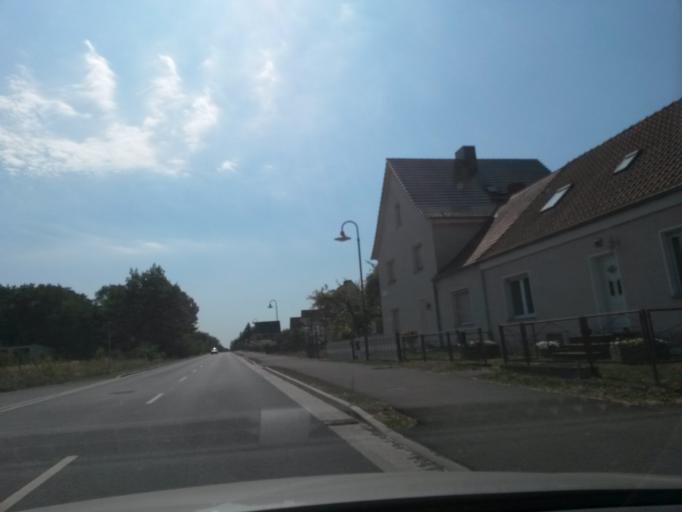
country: DE
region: Saxony-Anhalt
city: Jerichow
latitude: 52.4326
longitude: 11.9972
